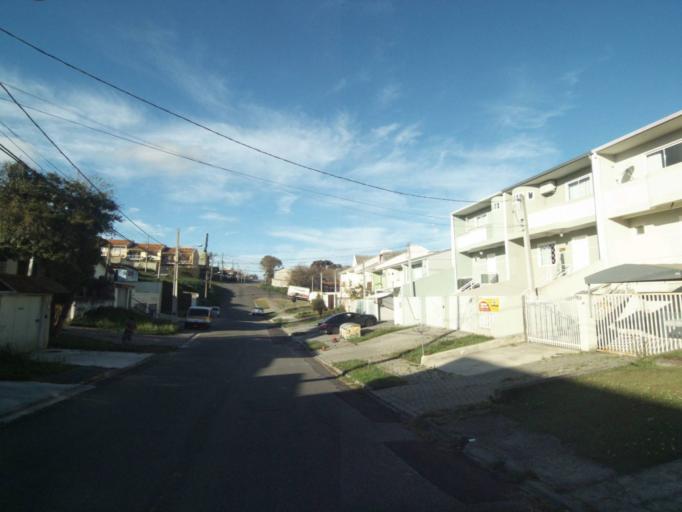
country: BR
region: Parana
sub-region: Curitiba
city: Curitiba
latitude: -25.3871
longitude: -49.2561
